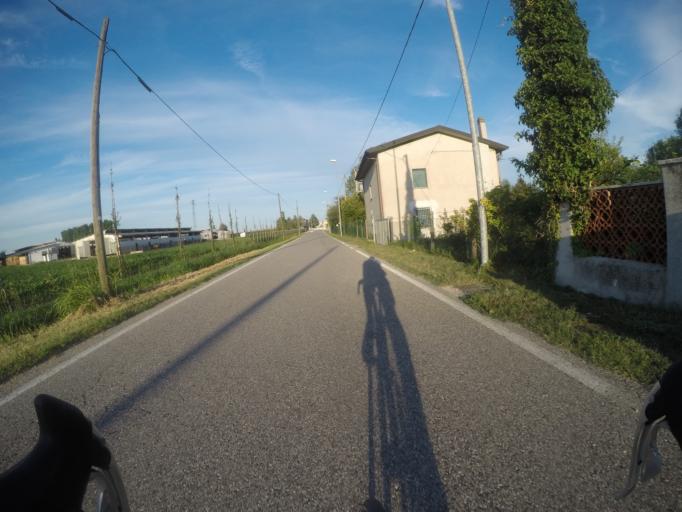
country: IT
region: Veneto
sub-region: Provincia di Rovigo
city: San Bellino
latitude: 45.0197
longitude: 11.5825
